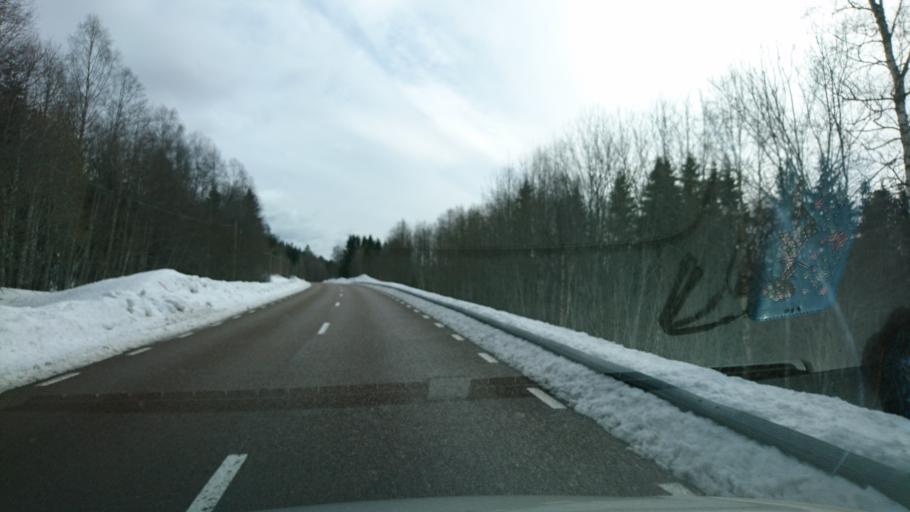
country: SE
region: Vaesternorrland
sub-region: Timra Kommun
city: Bergeforsen
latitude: 62.8104
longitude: 17.3870
